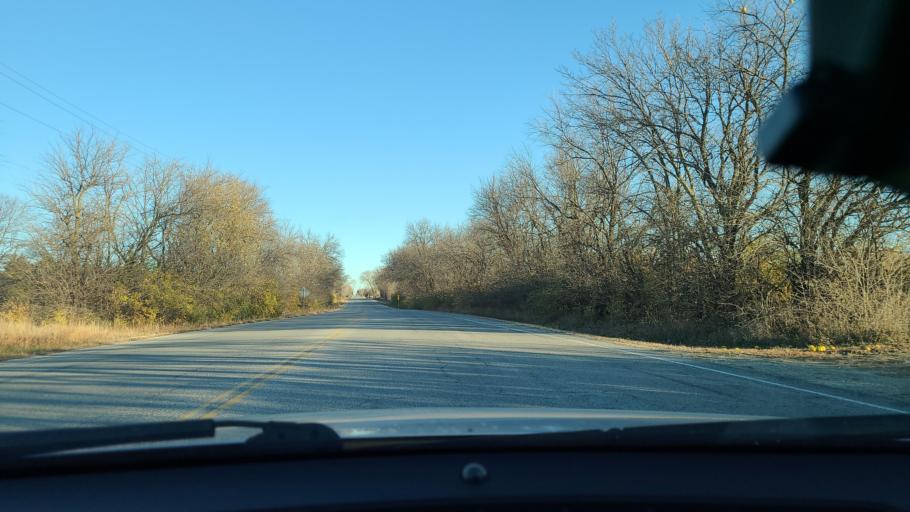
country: US
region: Kansas
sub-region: Sedgwick County
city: Park City
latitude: 37.8403
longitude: -97.3174
